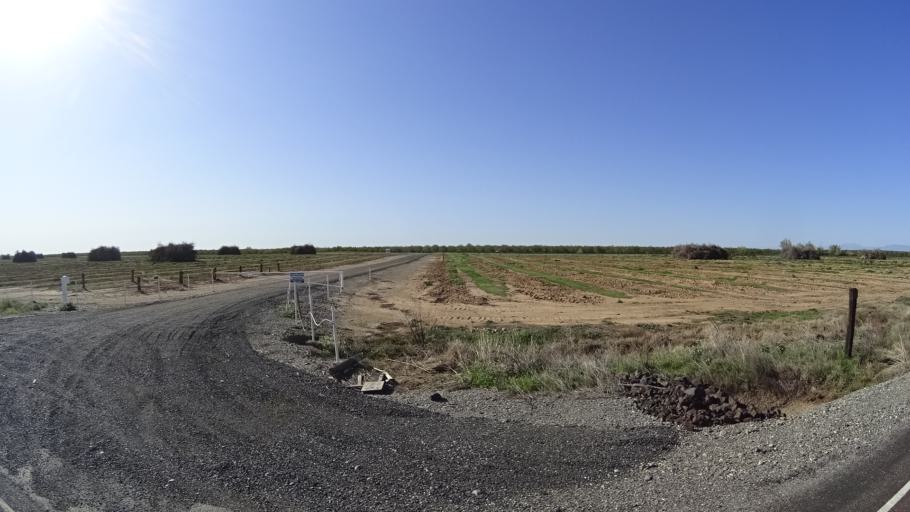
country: US
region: California
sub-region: Glenn County
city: Hamilton City
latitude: 39.7666
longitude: -122.0779
